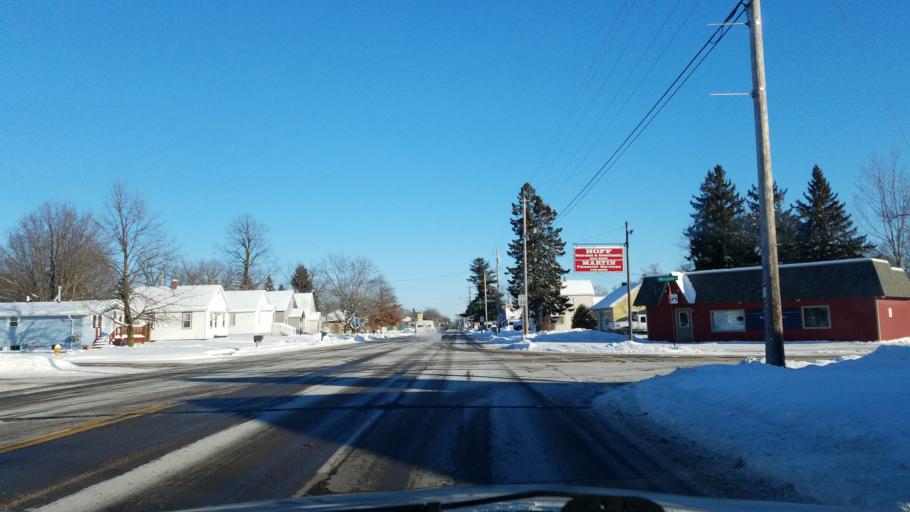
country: US
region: Wisconsin
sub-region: Barron County
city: Rice Lake
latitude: 45.5087
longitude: -91.7452
